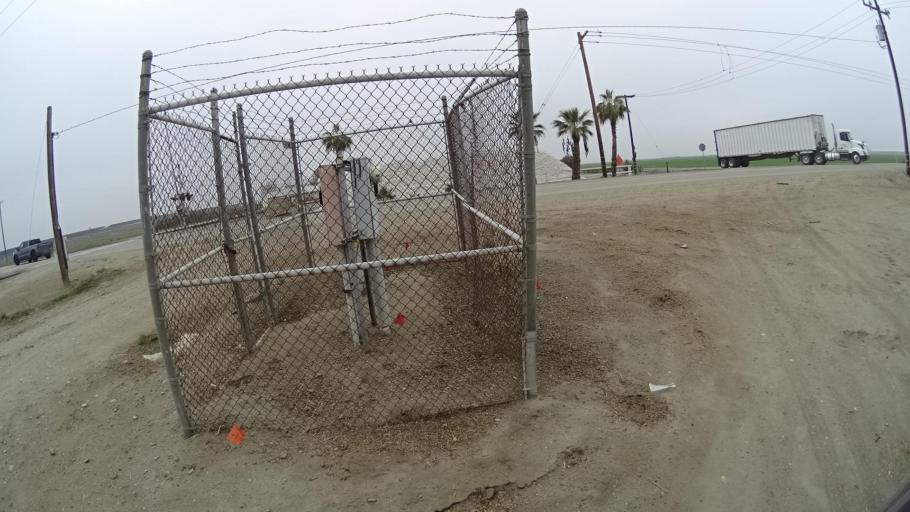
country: US
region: California
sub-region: Kern County
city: Greenfield
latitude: 35.1802
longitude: -119.1095
